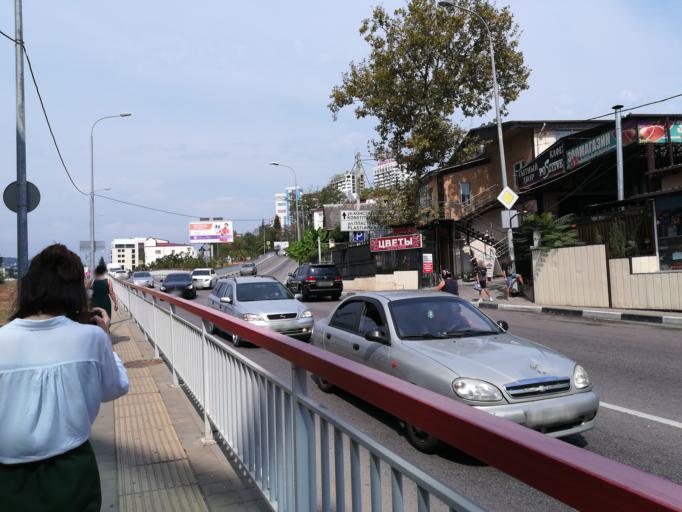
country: RU
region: Krasnodarskiy
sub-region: Sochi City
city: Sochi
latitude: 43.5969
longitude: 39.7316
